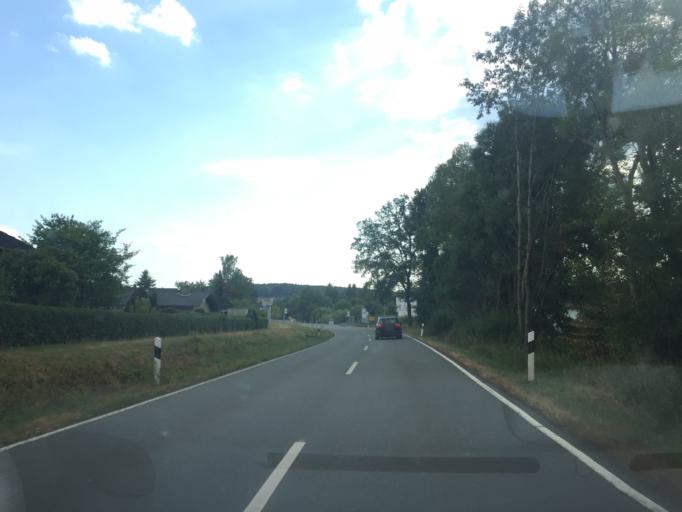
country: DE
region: Lower Saxony
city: Walkenried
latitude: 51.5945
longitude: 10.6194
